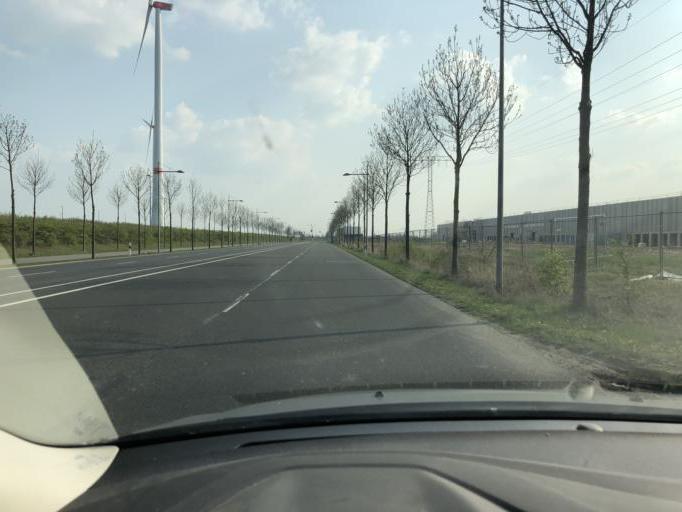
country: DE
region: Saxony
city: Rackwitz
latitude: 51.4066
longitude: 12.4322
